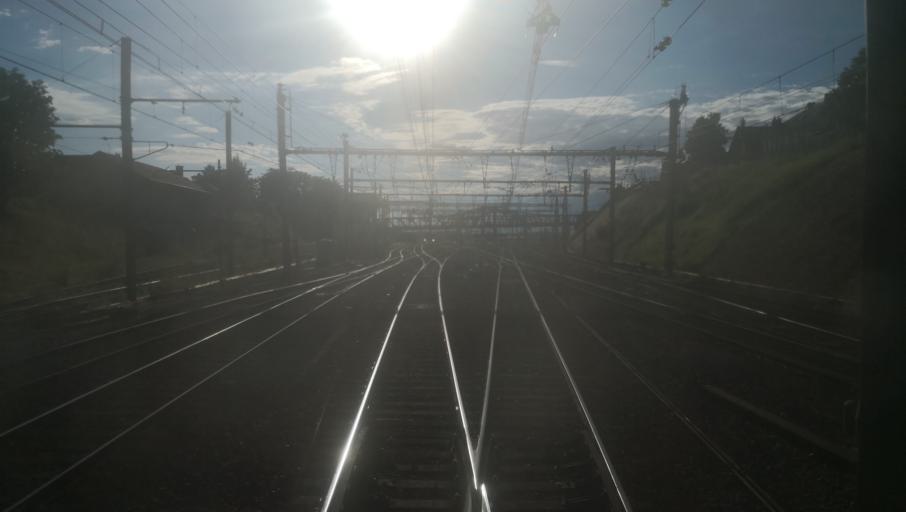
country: FR
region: Centre
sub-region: Departement du Cher
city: Vierzon
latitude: 47.2255
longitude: 2.0652
